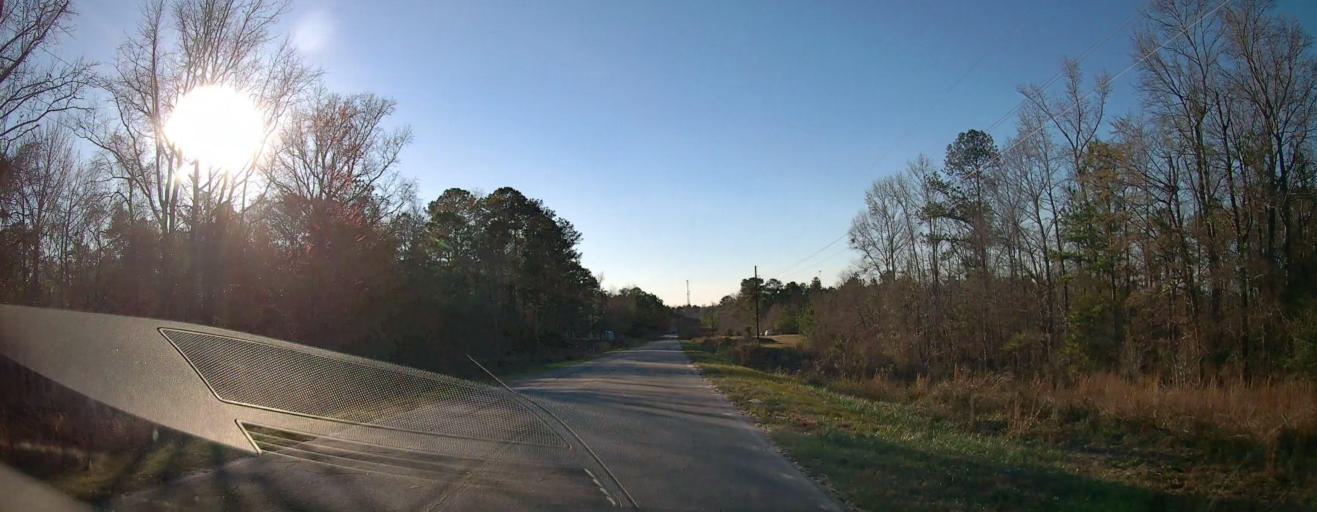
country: US
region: Georgia
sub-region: Talbot County
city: Talbotton
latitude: 32.5775
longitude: -84.5367
